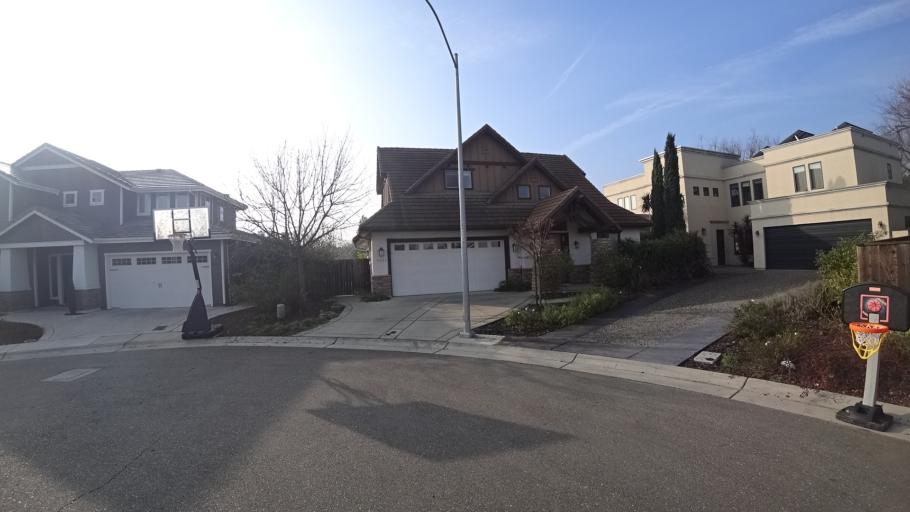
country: US
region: California
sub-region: Yolo County
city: Davis
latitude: 38.5686
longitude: -121.7648
